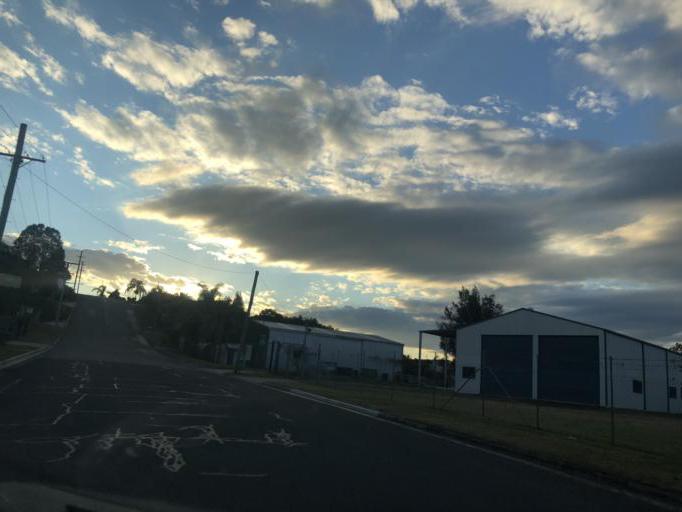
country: AU
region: New South Wales
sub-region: Nambucca Shire
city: Macksville
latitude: -30.7260
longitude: 152.9116
